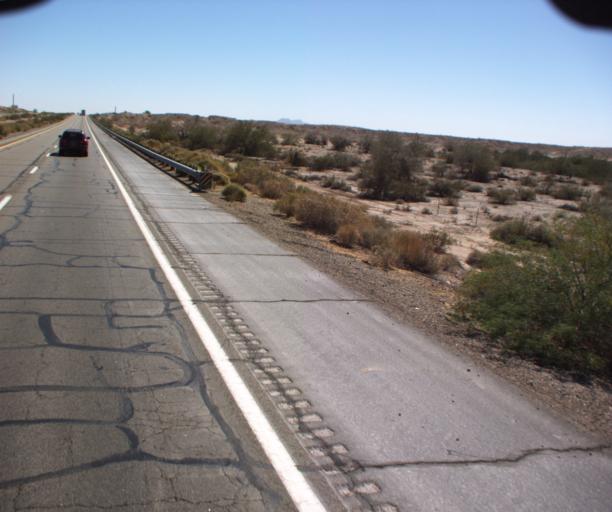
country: US
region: Arizona
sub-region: Yuma County
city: Wellton
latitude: 32.6631
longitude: -114.2684
